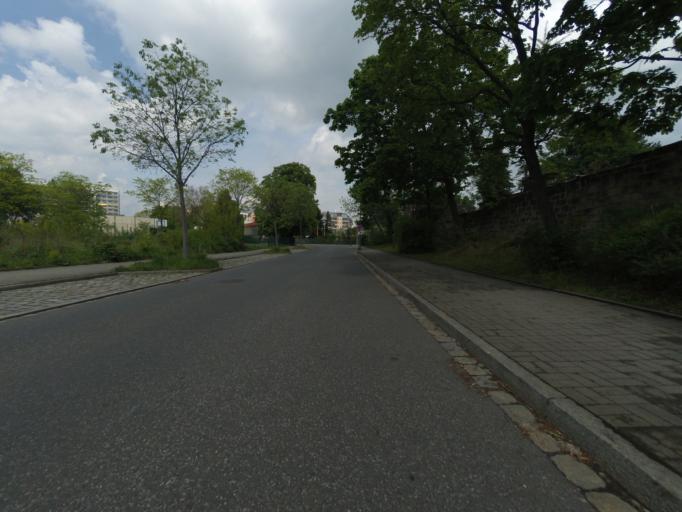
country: DE
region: Saxony
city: Albertstadt
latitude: 51.0551
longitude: 13.7698
